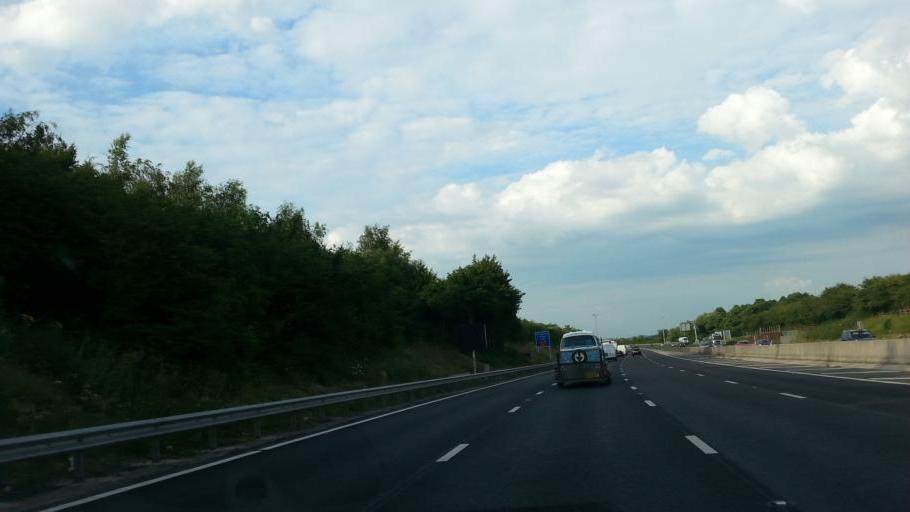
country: GB
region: England
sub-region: Worcestershire
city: Droitwich
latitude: 52.2680
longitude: -2.1321
